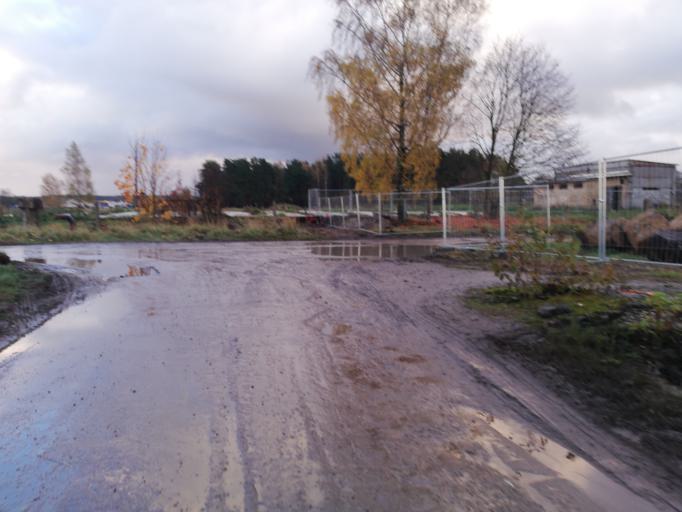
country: LV
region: Stopini
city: Ulbroka
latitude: 56.9526
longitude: 24.2365
